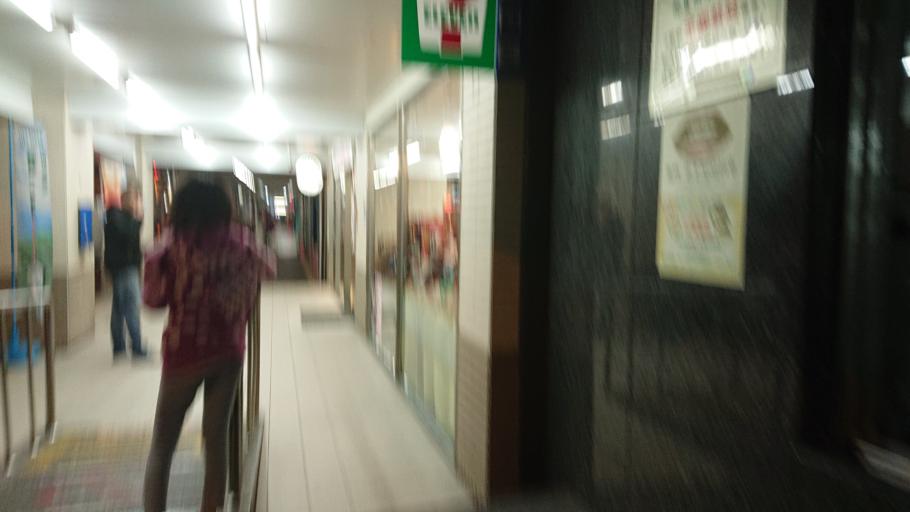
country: TW
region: Taiwan
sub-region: Tainan
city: Tainan
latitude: 22.9947
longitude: 120.1987
